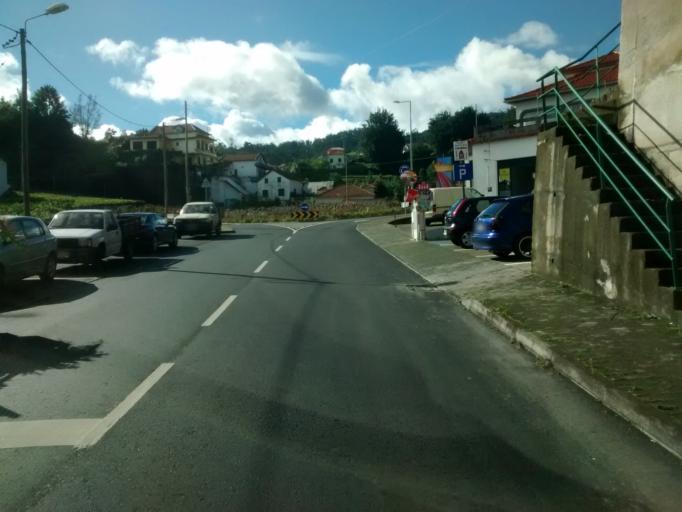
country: PT
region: Madeira
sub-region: Santana
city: Santana
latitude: 32.8059
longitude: -16.8850
